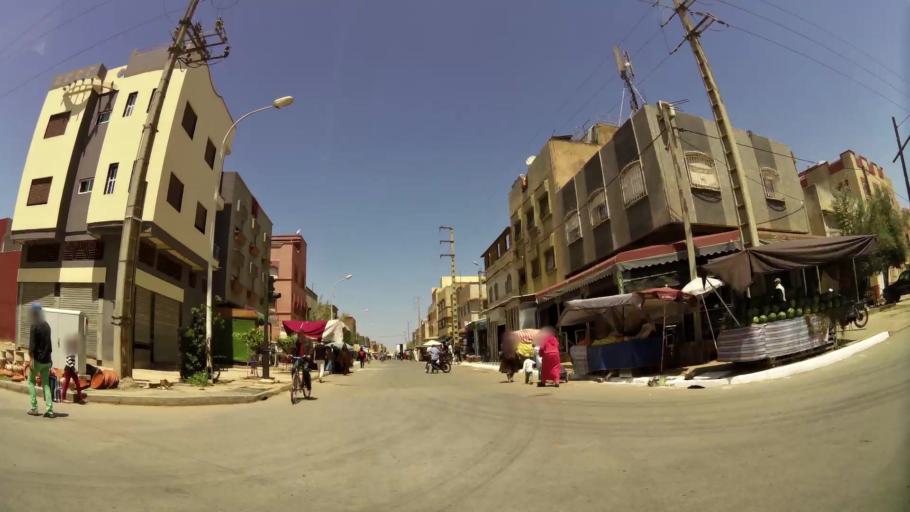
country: MA
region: Rabat-Sale-Zemmour-Zaer
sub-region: Khemisset
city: Khemisset
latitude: 33.8334
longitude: -6.0766
